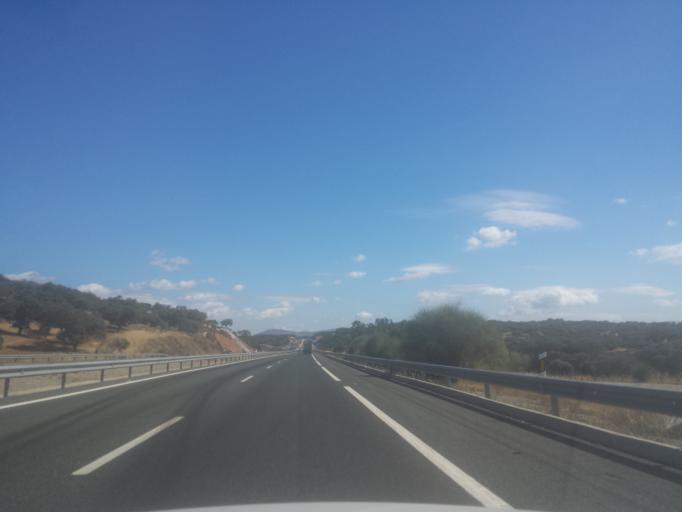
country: ES
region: Andalusia
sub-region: Provincia de Huelva
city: Santa Olalla del Cala
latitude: 37.8807
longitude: -6.2201
